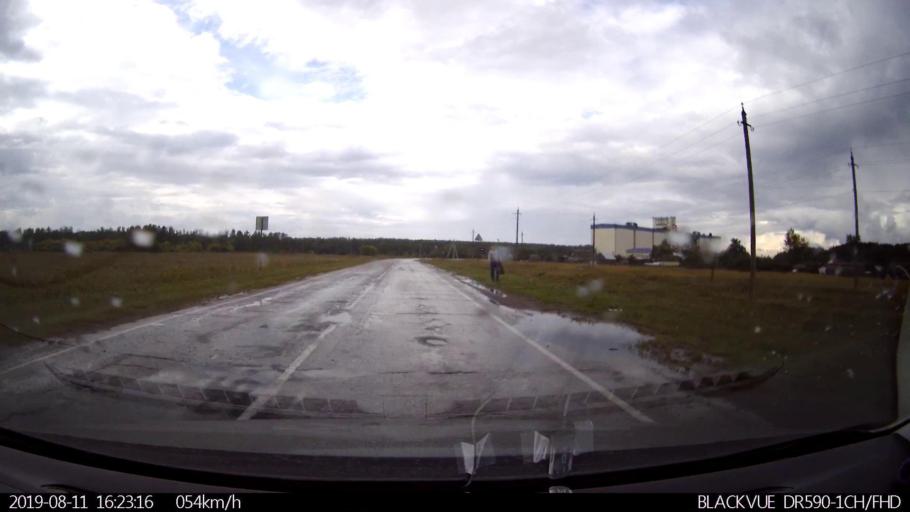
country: RU
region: Ulyanovsk
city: Mayna
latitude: 54.0940
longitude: 47.5892
